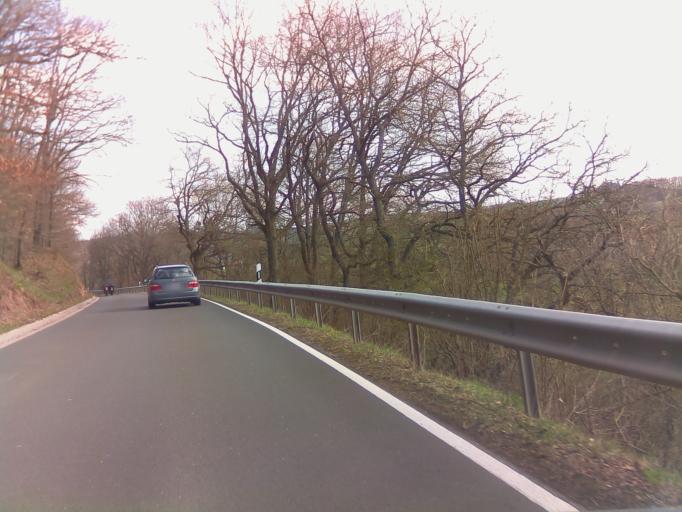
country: DE
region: Rheinland-Pfalz
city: Schmidthachenbach
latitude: 49.7371
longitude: 7.4588
